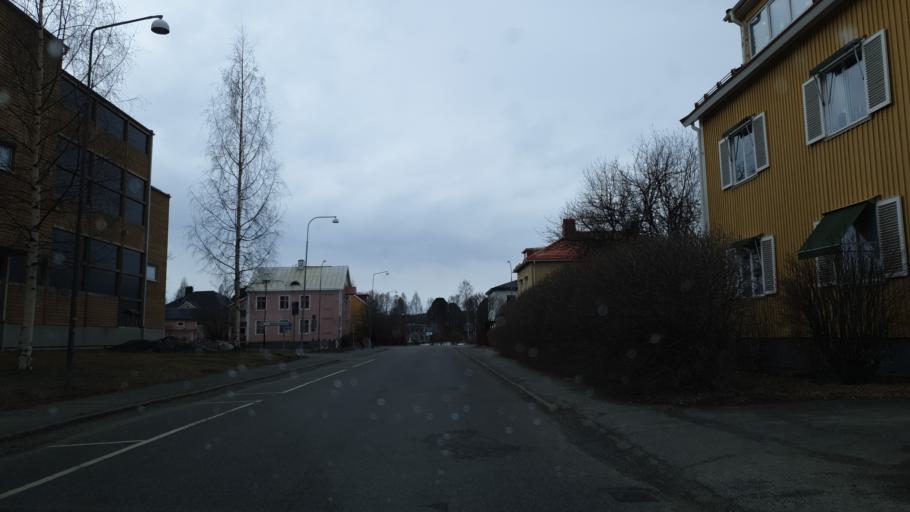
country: SE
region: Vaesterbotten
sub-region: Skelleftea Kommun
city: Skelleftea
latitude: 64.7523
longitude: 20.9403
